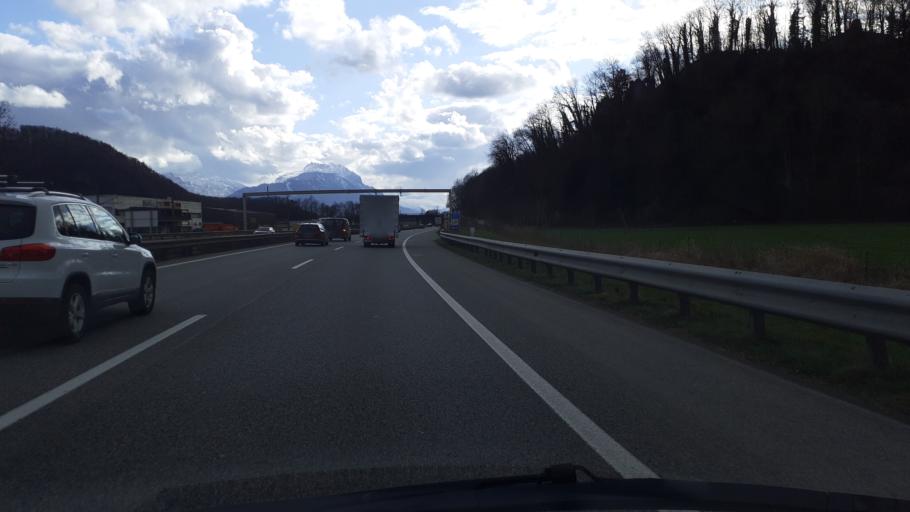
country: AT
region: Vorarlberg
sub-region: Politischer Bezirk Feldkirch
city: Gotzis
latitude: 47.3266
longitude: 9.6273
